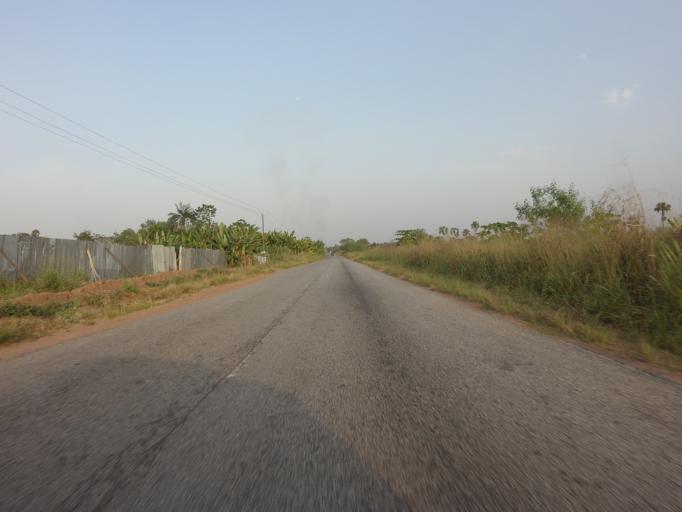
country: GH
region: Volta
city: Ho
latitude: 6.5730
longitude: 0.3687
